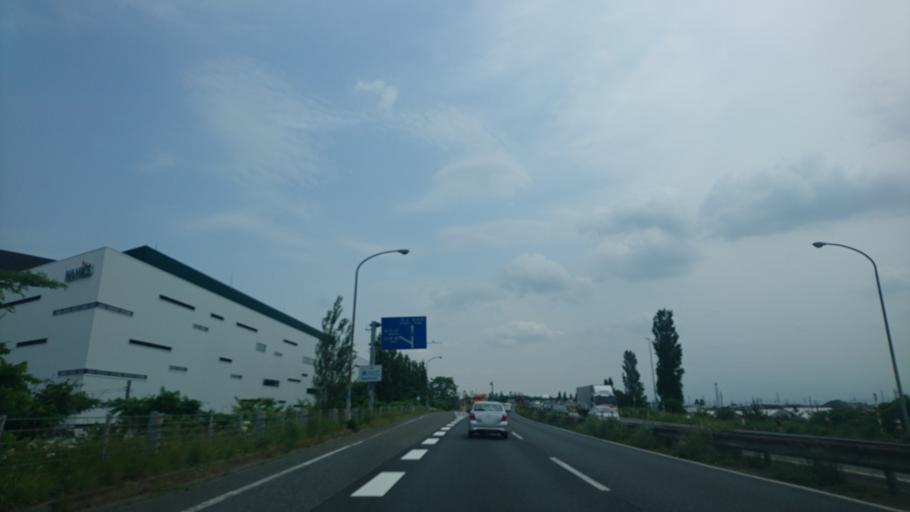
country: JP
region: Niigata
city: Kameda-honcho
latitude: 37.9359
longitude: 139.1533
